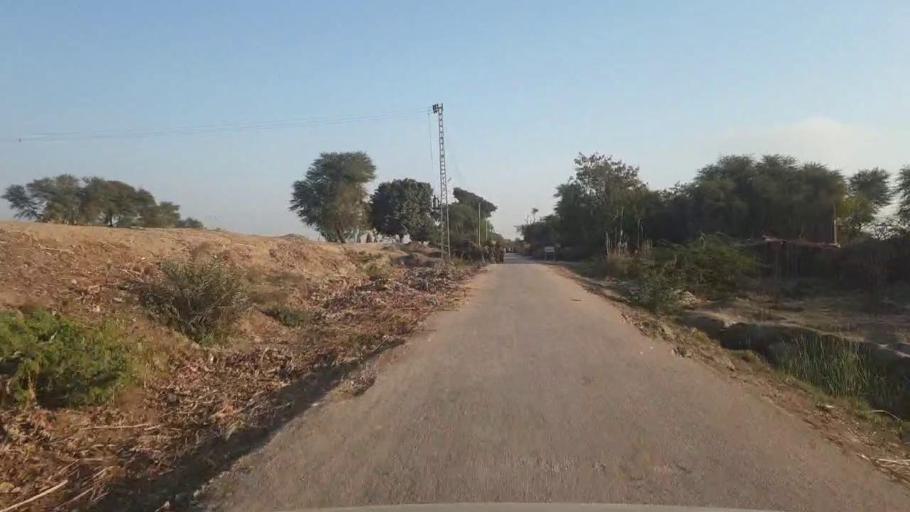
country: PK
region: Sindh
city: Chambar
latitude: 25.2888
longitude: 68.8961
